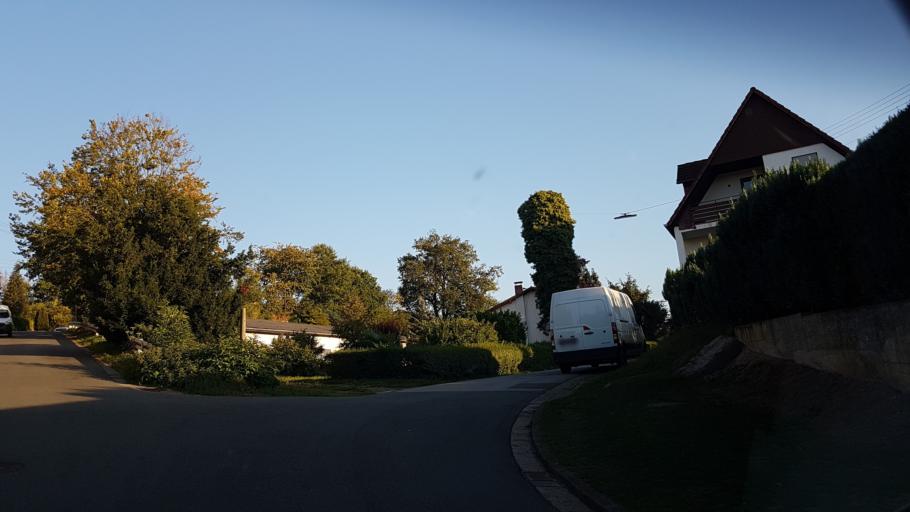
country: DE
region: Saarland
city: Illingen
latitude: 49.4145
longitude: 7.0163
